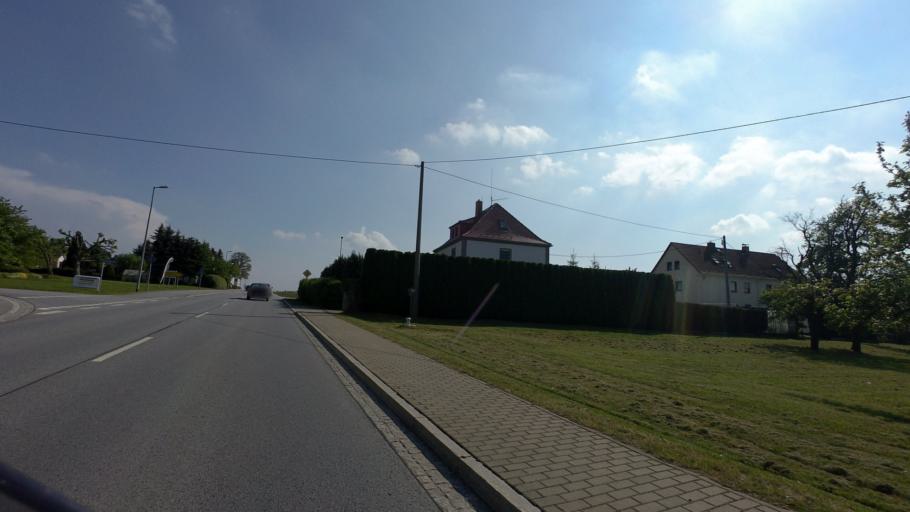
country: DE
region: Saxony
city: Grosspostwitz
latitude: 51.1367
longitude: 14.4416
